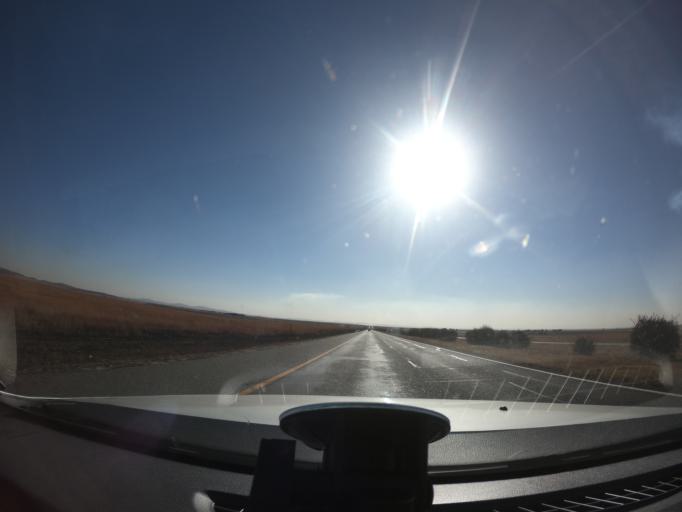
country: ZA
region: Gauteng
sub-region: Sedibeng District Municipality
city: Heidelberg
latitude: -26.4296
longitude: 28.2924
